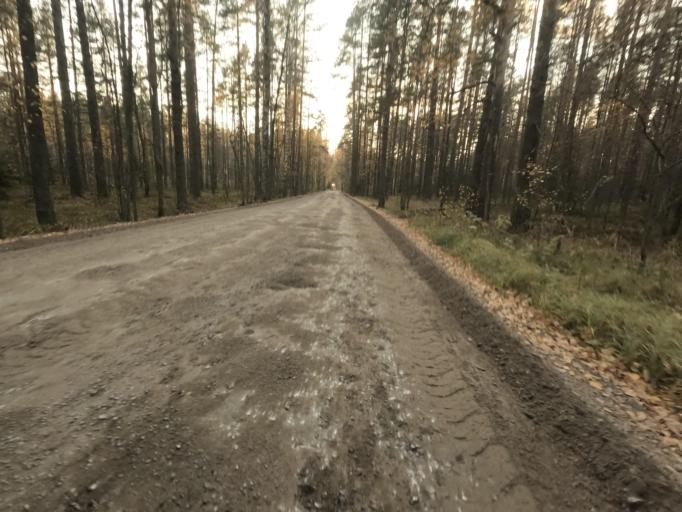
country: RU
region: St.-Petersburg
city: Repino
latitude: 60.1870
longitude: 29.8733
